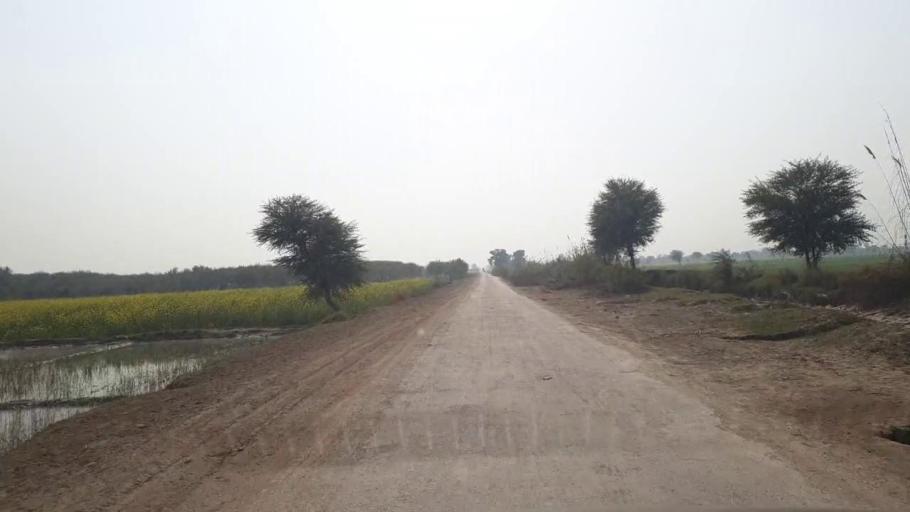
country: PK
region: Sindh
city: Hala
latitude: 25.9173
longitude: 68.4458
